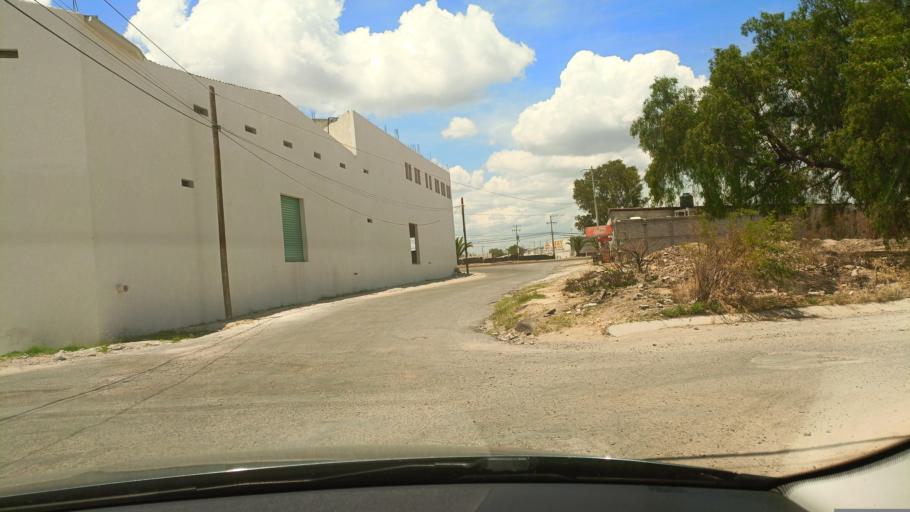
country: MX
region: Guanajuato
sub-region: San Luis de la Paz
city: San Ignacio
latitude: 21.2952
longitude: -100.5336
